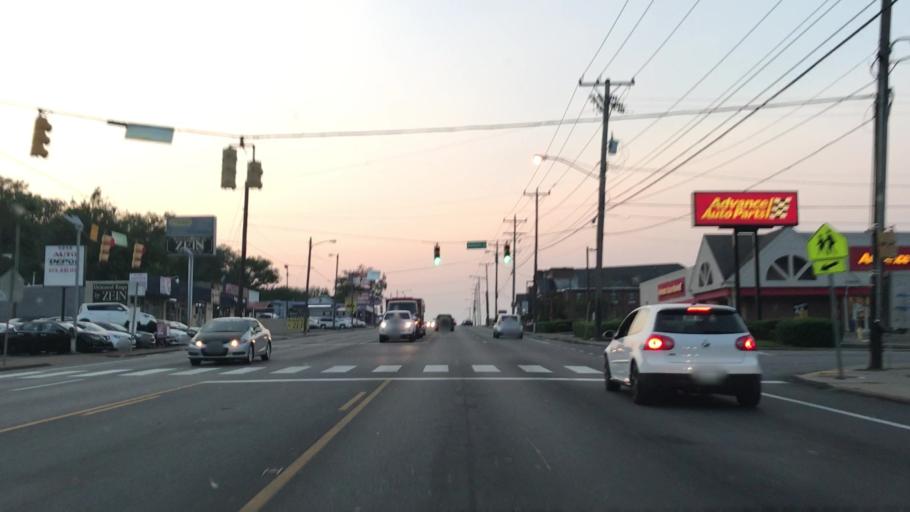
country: US
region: Tennessee
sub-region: Davidson County
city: Oak Hill
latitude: 36.1016
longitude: -86.7404
